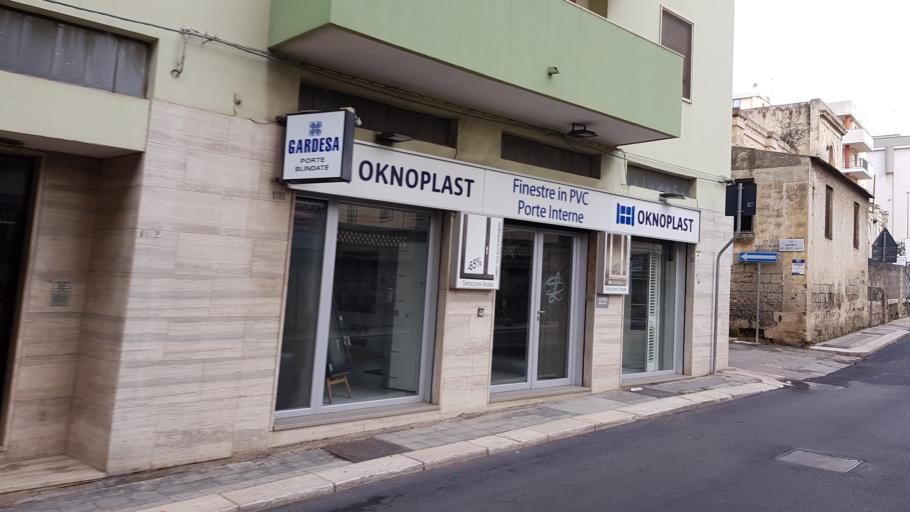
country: IT
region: Apulia
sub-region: Provincia di Brindisi
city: Brindisi
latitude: 40.6375
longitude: 17.9303
